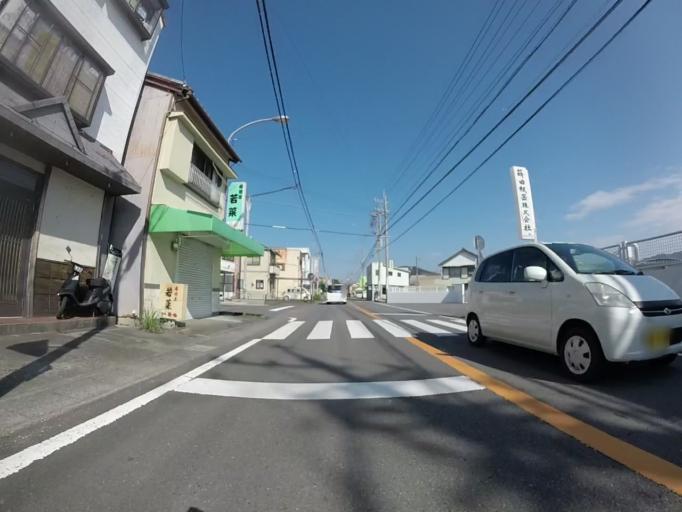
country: JP
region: Shizuoka
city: Fujieda
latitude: 34.8777
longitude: 138.2650
